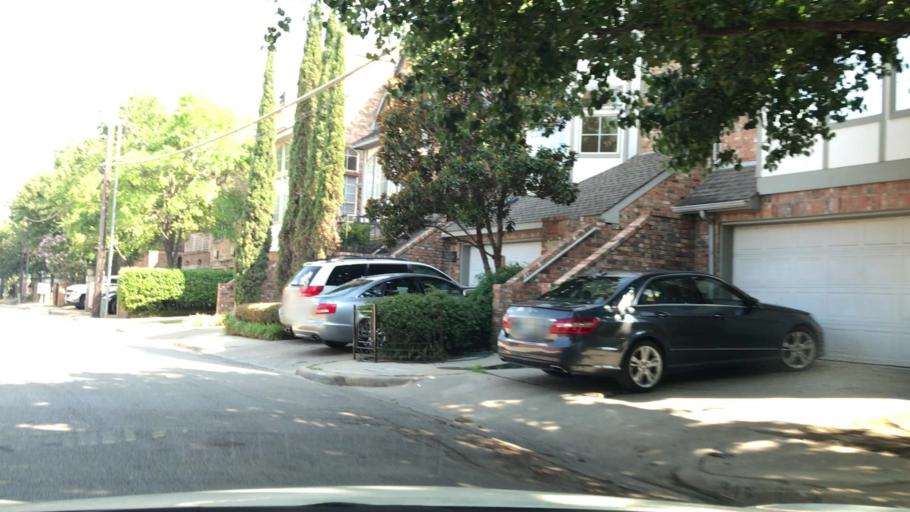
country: US
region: Texas
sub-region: Dallas County
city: Dallas
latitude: 32.7926
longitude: -96.7905
